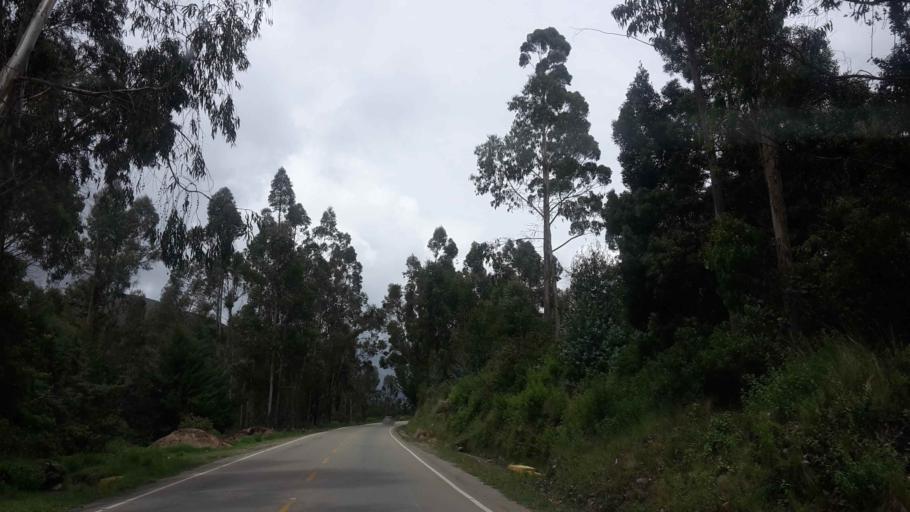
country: BO
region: Cochabamba
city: Arani
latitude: -17.4779
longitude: -65.4894
